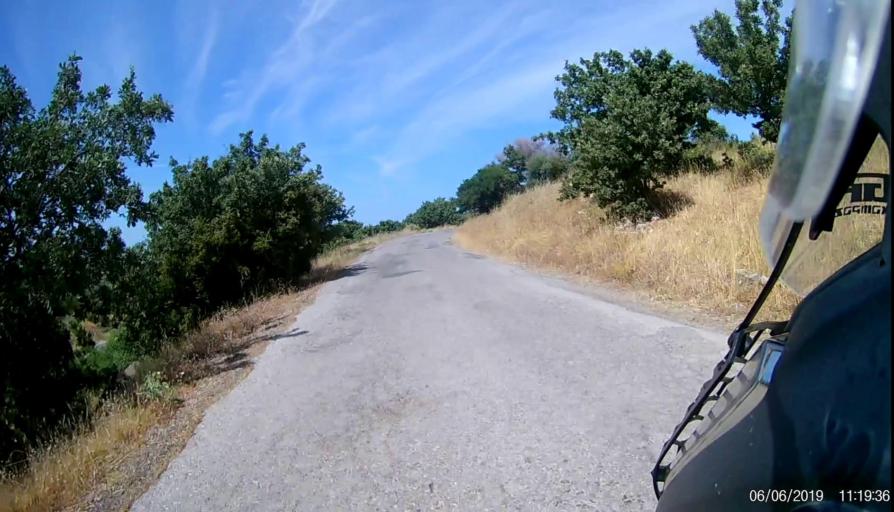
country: TR
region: Canakkale
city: Gulpinar
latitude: 39.6590
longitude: 26.1636
